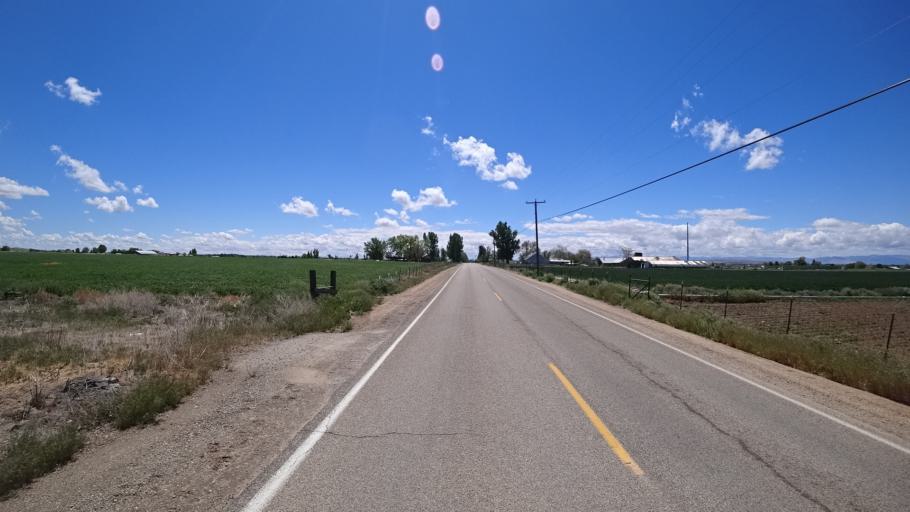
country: US
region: Idaho
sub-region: Ada County
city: Kuna
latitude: 43.5302
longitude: -116.3543
